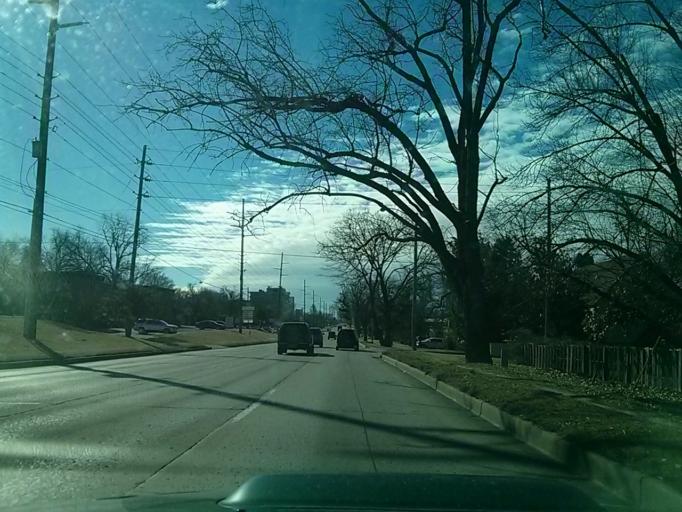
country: US
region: Oklahoma
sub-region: Tulsa County
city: Jenks
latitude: 36.0849
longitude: -95.9581
